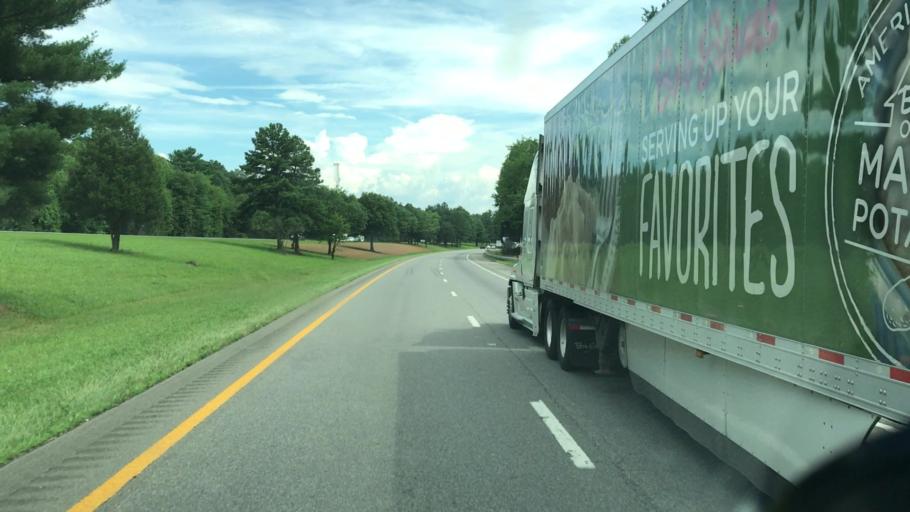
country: US
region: North Carolina
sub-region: Surry County
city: Dobson
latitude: 36.3489
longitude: -80.7961
